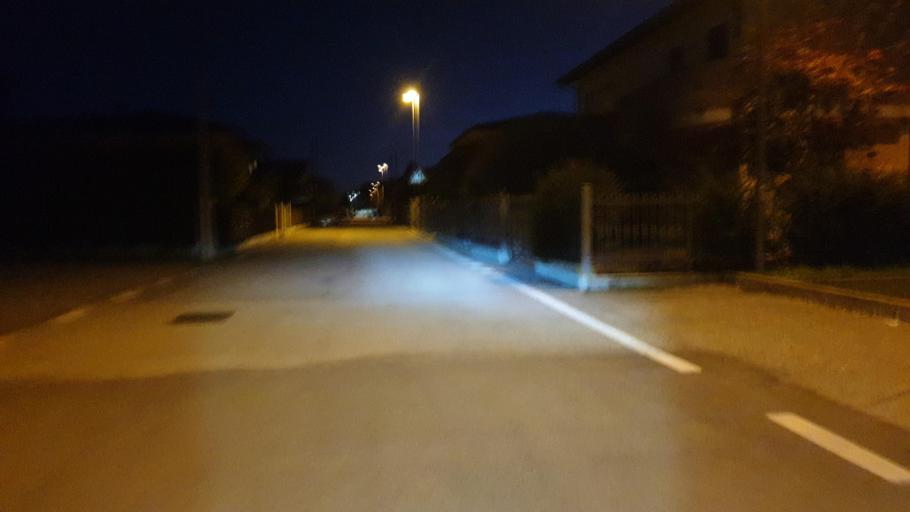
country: IT
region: Veneto
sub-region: Provincia di Venezia
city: Tombelle
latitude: 45.3988
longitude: 11.9778
